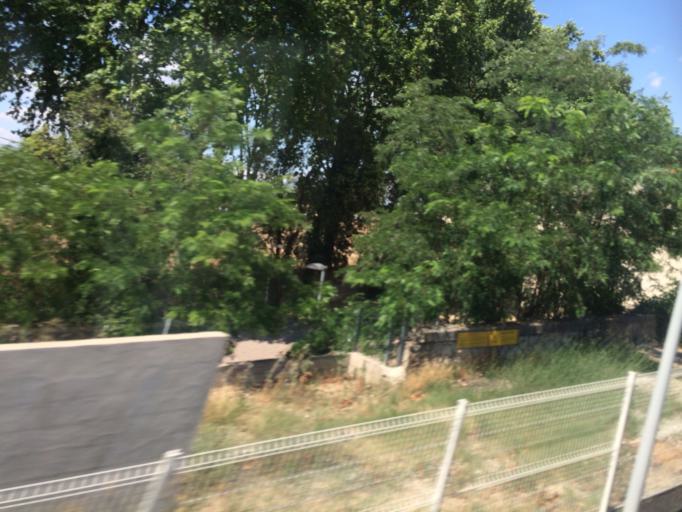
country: FR
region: Languedoc-Roussillon
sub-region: Departement de l'Herault
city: Baillargues
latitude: 43.6531
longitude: 4.0062
